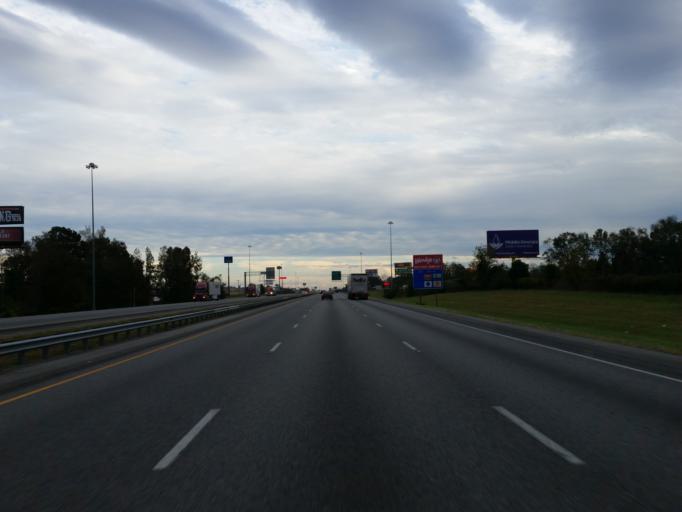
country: US
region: Georgia
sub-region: Lowndes County
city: Remerton
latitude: 30.8314
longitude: -83.3243
